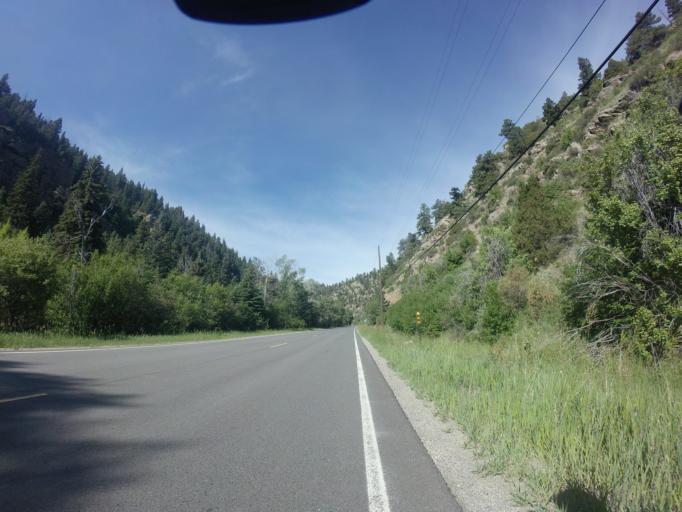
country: US
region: Colorado
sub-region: Clear Creek County
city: Idaho Springs
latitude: 39.7221
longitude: -105.5656
